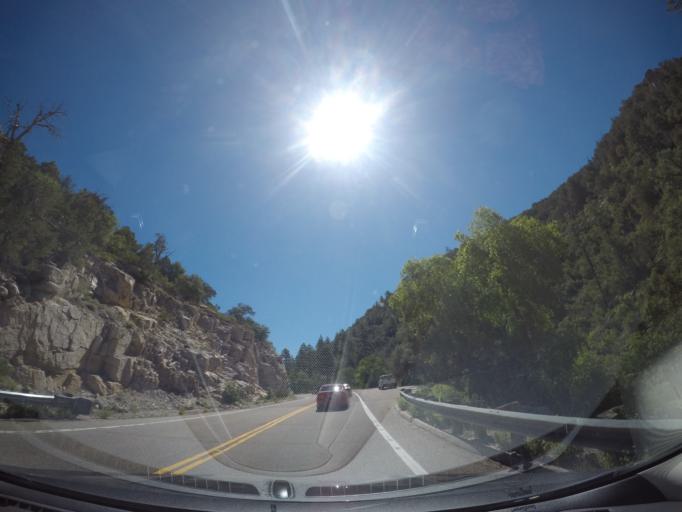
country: US
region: Arizona
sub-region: Pima County
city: Tanque Verde
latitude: 32.3710
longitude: -110.7009
